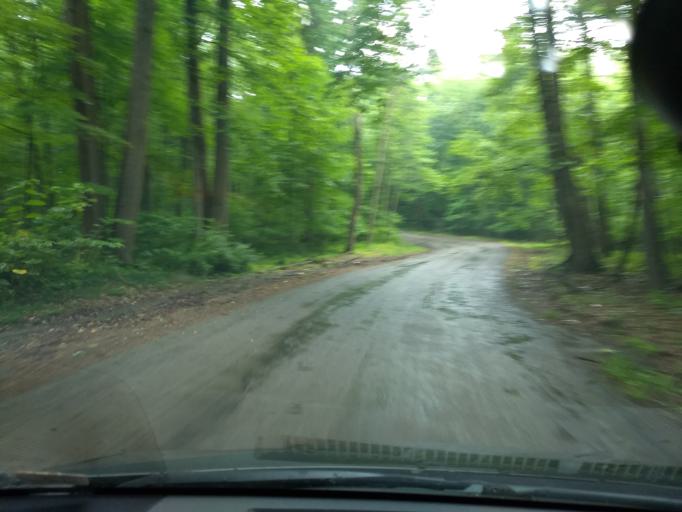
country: US
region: Pennsylvania
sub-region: Armstrong County
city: Orchard Hills
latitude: 40.5552
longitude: -79.5067
